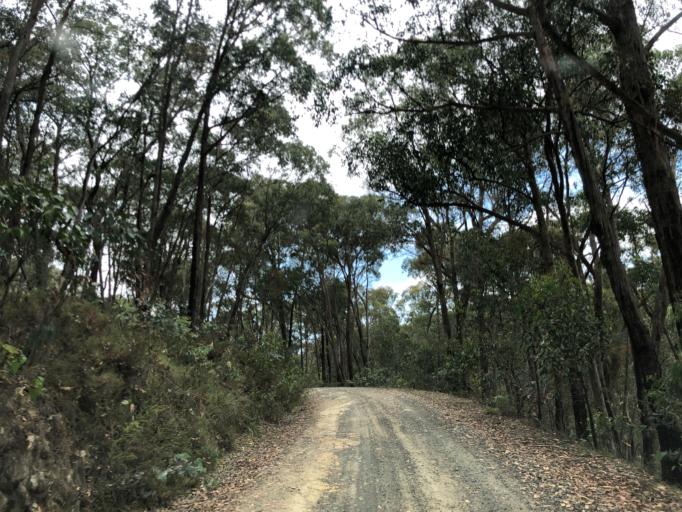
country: AU
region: Victoria
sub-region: Moorabool
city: Bacchus Marsh
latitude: -37.4601
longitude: 144.2749
